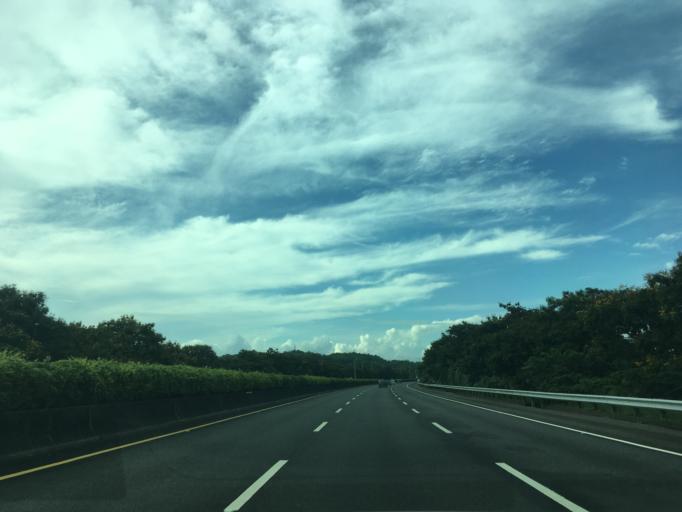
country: TW
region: Taiwan
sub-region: Chiayi
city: Jiayi Shi
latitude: 23.5171
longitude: 120.4850
